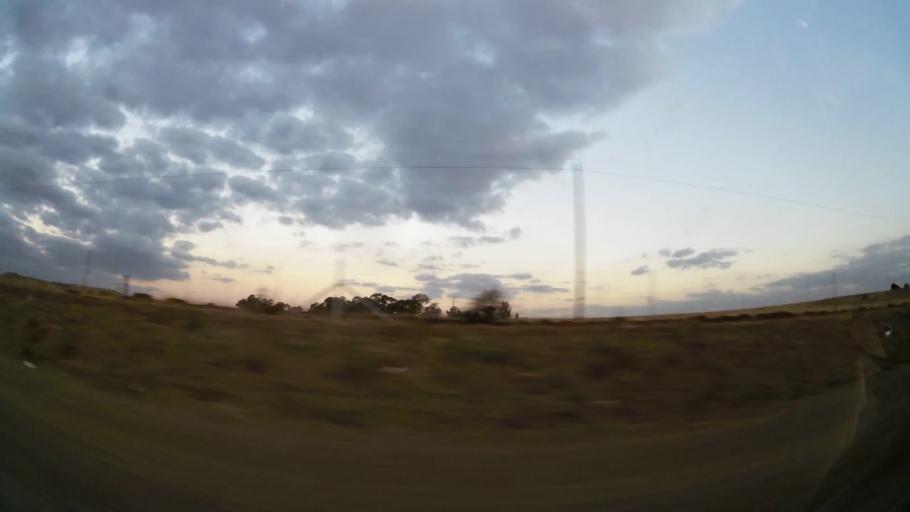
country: ZA
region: Gauteng
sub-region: West Rand District Municipality
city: Krugersdorp
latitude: -26.0597
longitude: 27.7022
